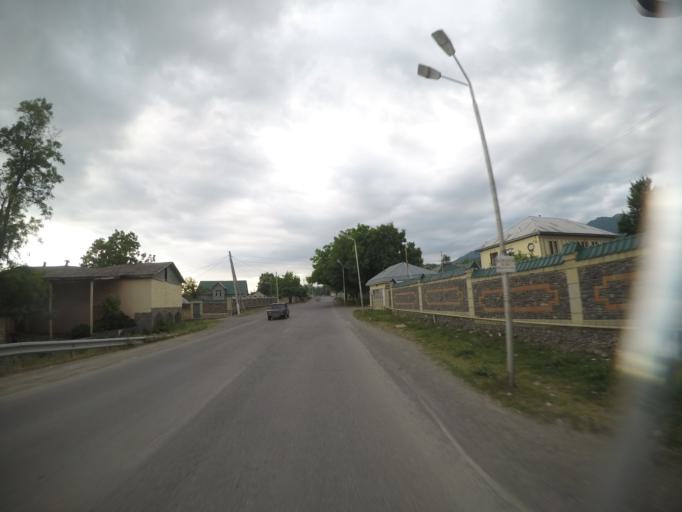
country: AZ
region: Qabala Rayon
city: Qutqashen
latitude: 40.9470
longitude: 47.9412
